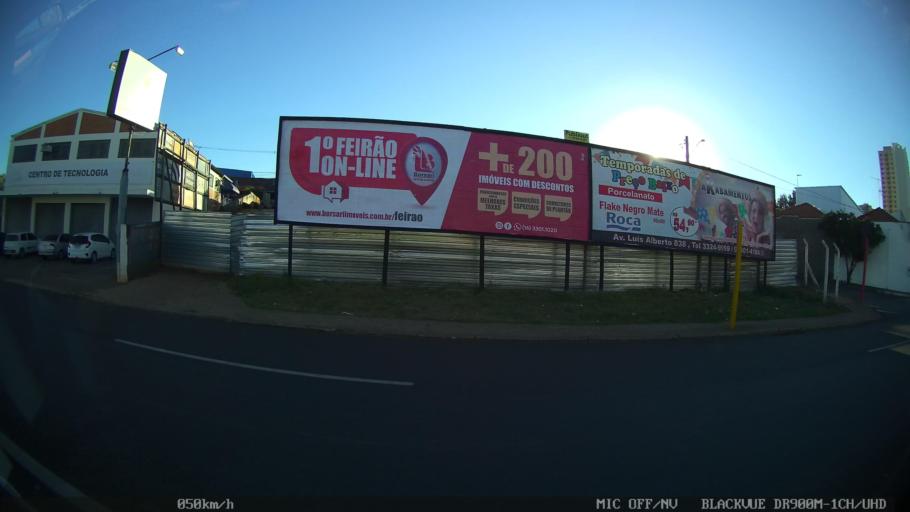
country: BR
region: Sao Paulo
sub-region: Araraquara
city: Araraquara
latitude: -21.8004
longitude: -48.1732
